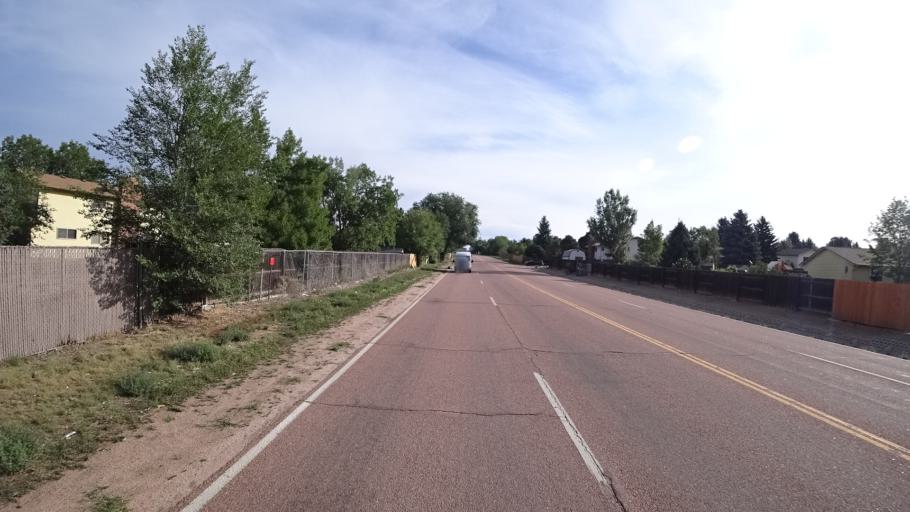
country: US
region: Colorado
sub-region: El Paso County
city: Security-Widefield
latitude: 38.7322
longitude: -104.6962
